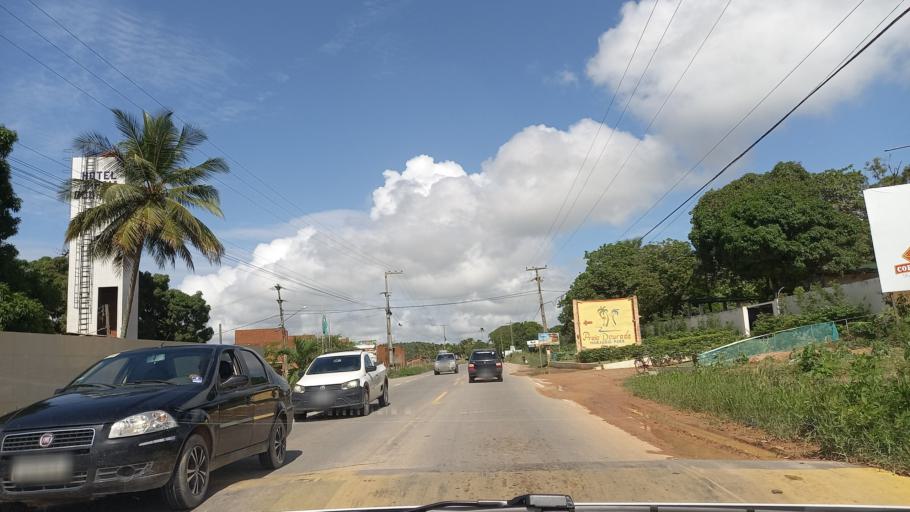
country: BR
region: Alagoas
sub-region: Maragogi
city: Maragogi
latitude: -8.9913
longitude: -35.2041
